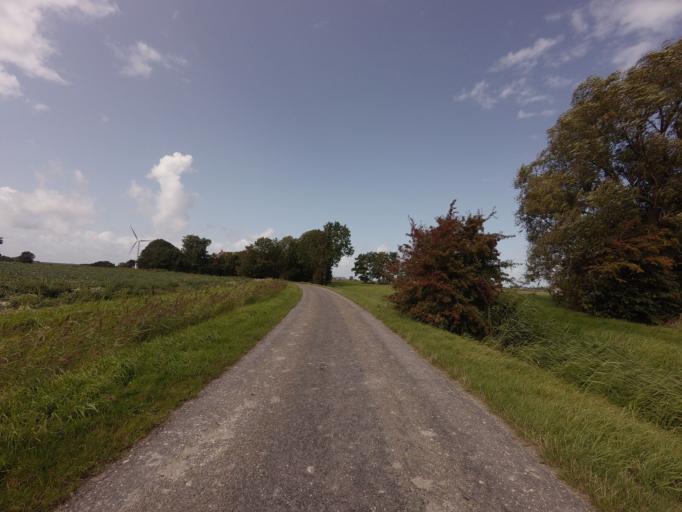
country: NL
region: Friesland
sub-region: Gemeente Harlingen
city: Harlingen
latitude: 53.1222
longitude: 5.4413
